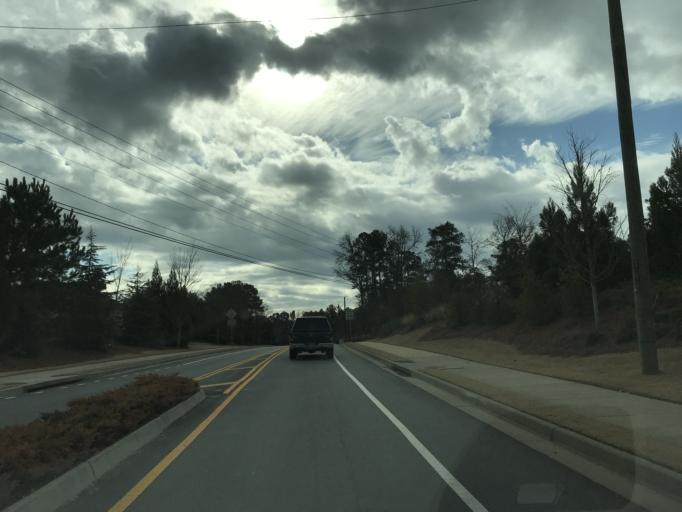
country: US
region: Georgia
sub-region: Fulton County
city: Alpharetta
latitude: 34.0919
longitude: -84.3130
